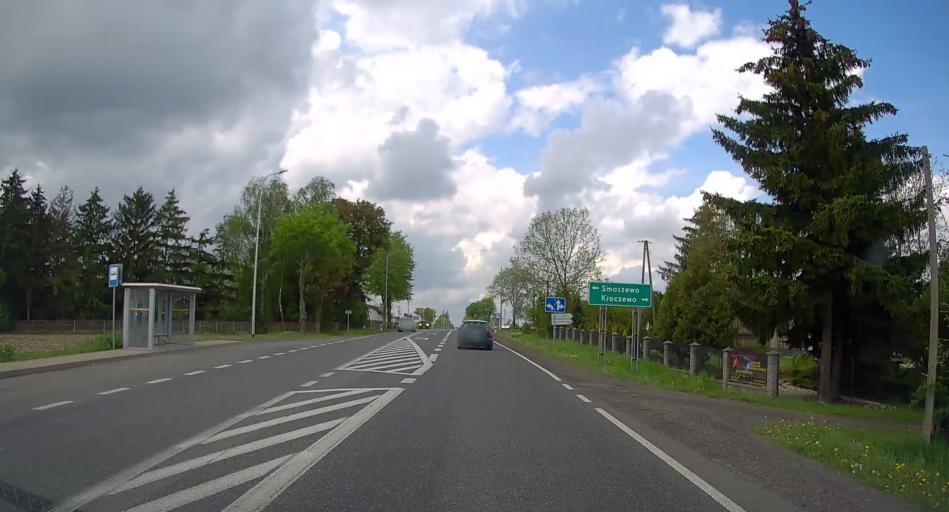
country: PL
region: Masovian Voivodeship
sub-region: Powiat plonski
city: Zaluski
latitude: 52.4443
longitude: 20.5248
